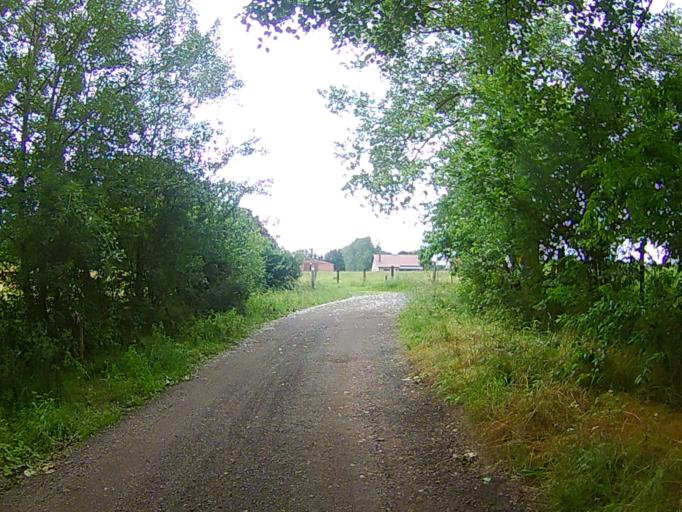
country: BE
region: Flanders
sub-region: Provincie Antwerpen
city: Berlaar
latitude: 51.1168
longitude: 4.6920
